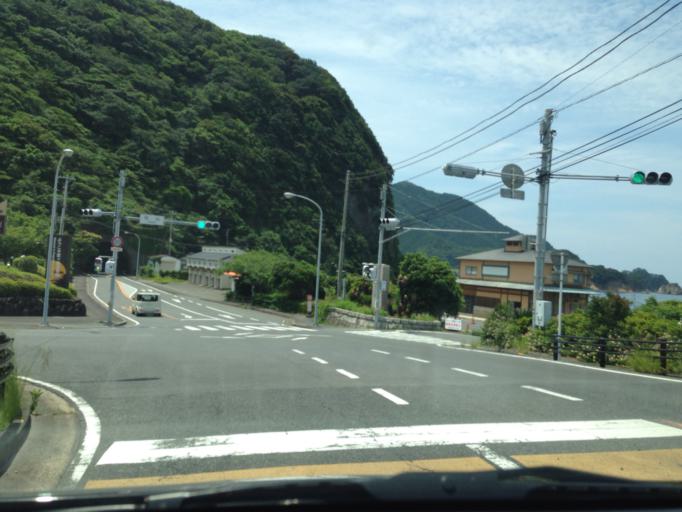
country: JP
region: Shizuoka
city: Heda
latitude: 34.8550
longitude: 138.7772
